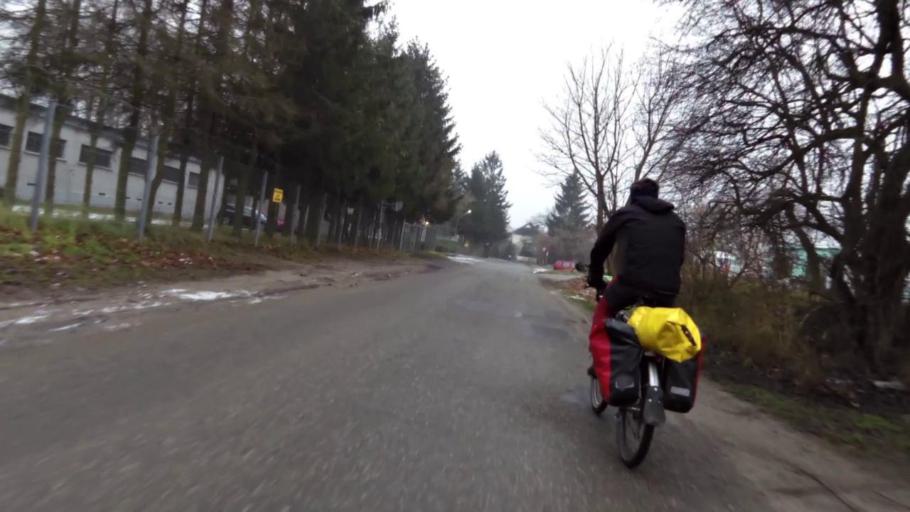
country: PL
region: West Pomeranian Voivodeship
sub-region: Powiat walecki
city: Walcz
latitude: 53.2832
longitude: 16.4728
